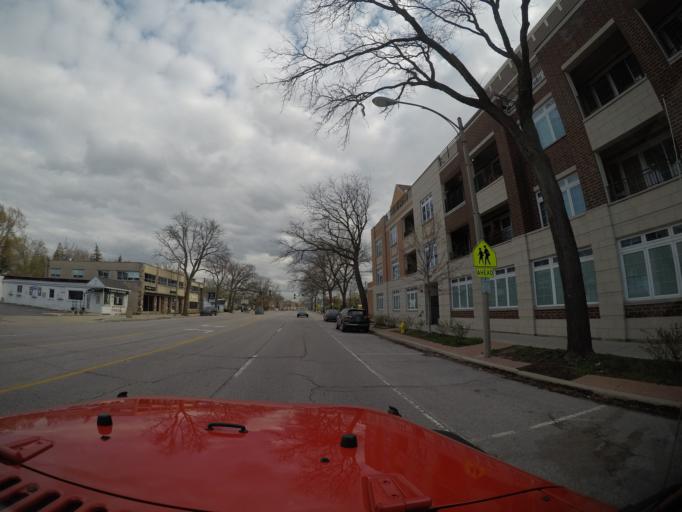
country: US
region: Illinois
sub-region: Cook County
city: Glenview
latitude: 42.0762
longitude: -87.7987
